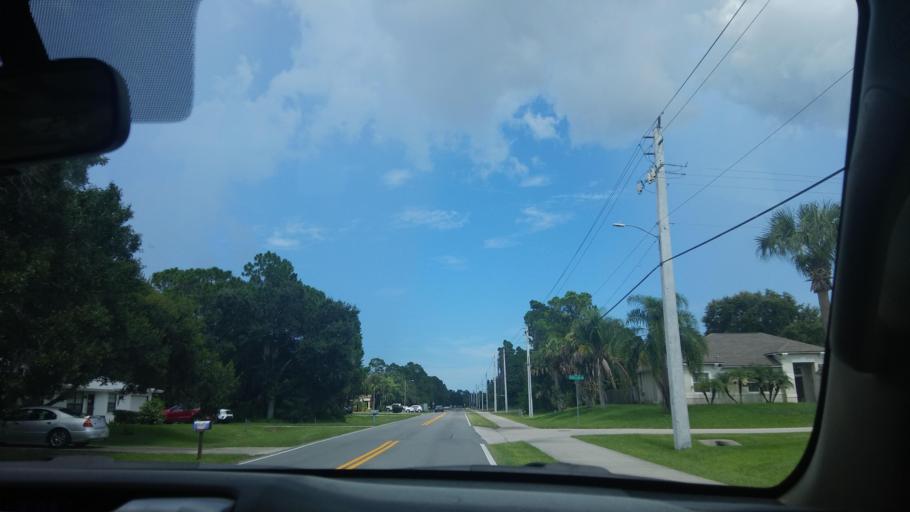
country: US
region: Florida
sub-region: Brevard County
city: June Park
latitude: 28.0109
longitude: -80.6693
